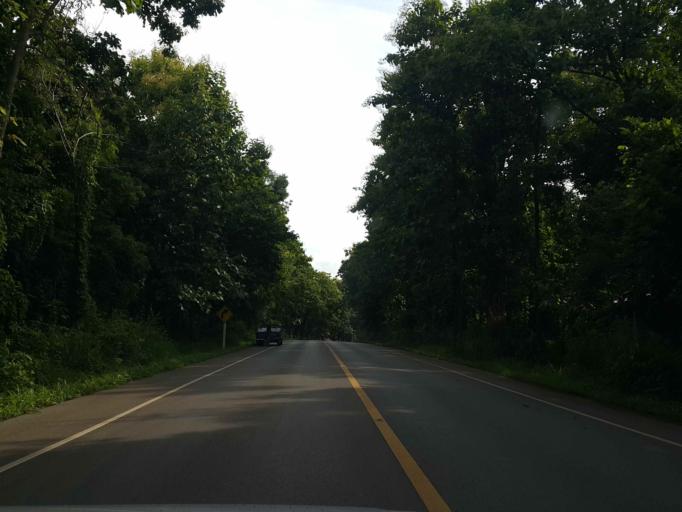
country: TH
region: Phrae
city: Den Chai
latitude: 17.8381
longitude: 99.8730
